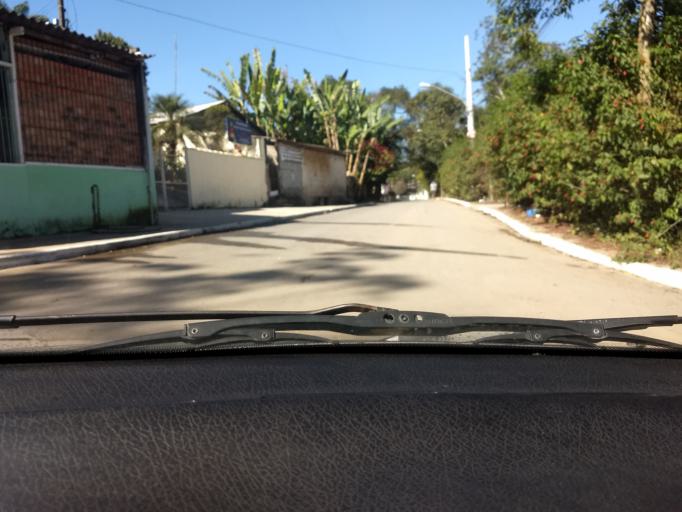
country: BR
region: Sao Paulo
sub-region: Embu-Guacu
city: Embu Guacu
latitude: -23.8086
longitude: -46.7656
